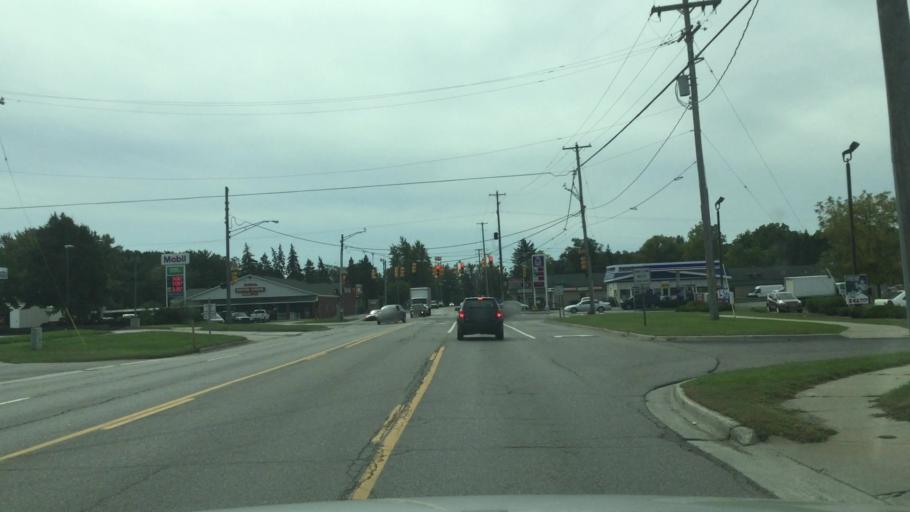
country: US
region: Michigan
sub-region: Oakland County
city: Holly
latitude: 42.8072
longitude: -83.6282
